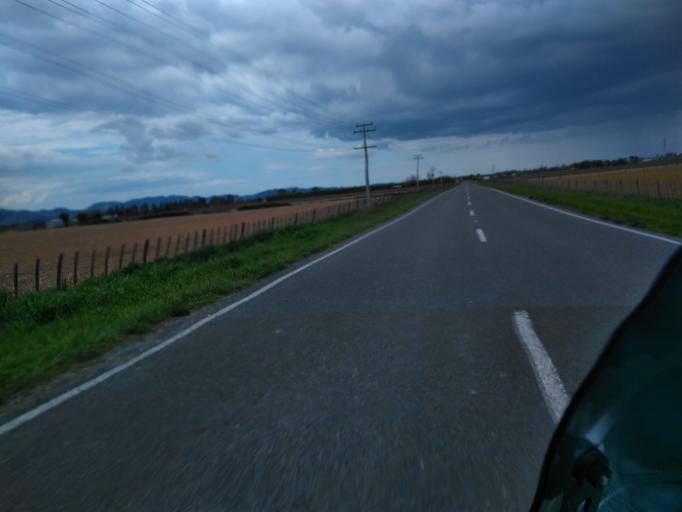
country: NZ
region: Gisborne
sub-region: Gisborne District
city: Gisborne
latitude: -38.6421
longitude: 177.8899
